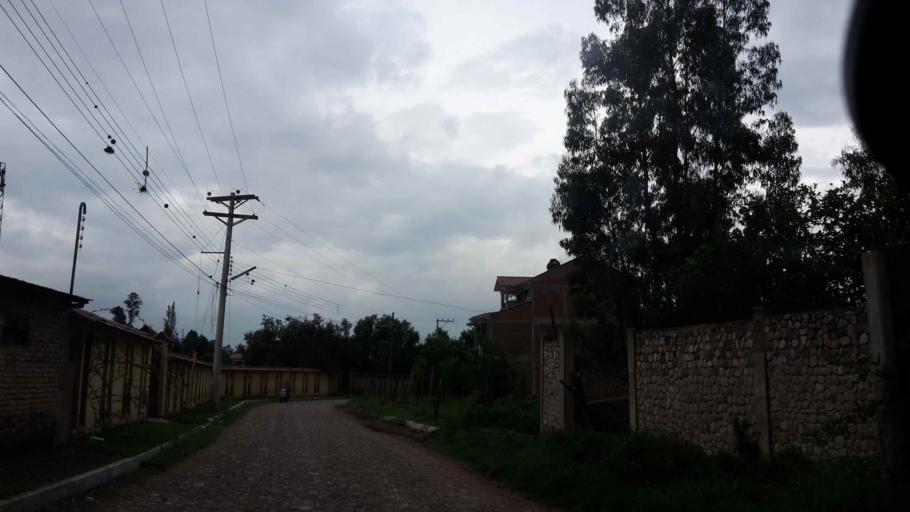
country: BO
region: Cochabamba
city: Cochabamba
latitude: -17.3609
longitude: -66.2139
